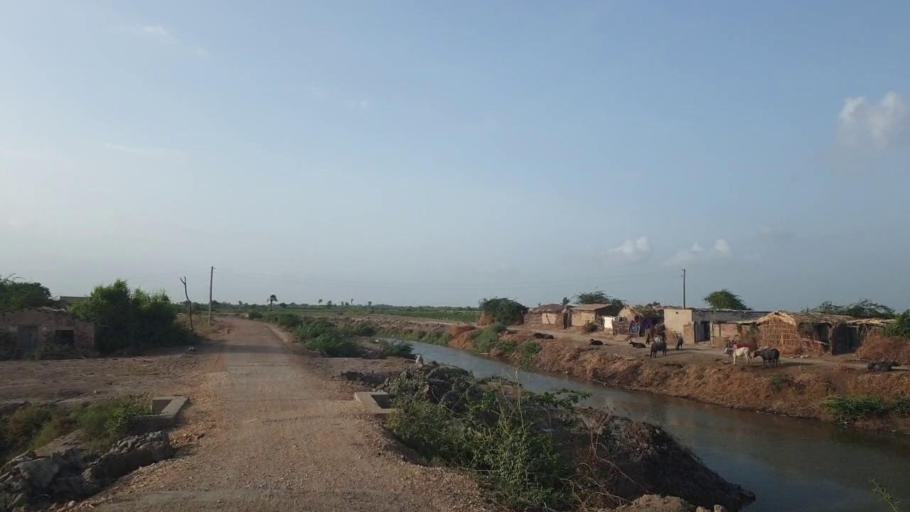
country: PK
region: Sindh
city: Kadhan
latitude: 24.6277
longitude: 69.1600
